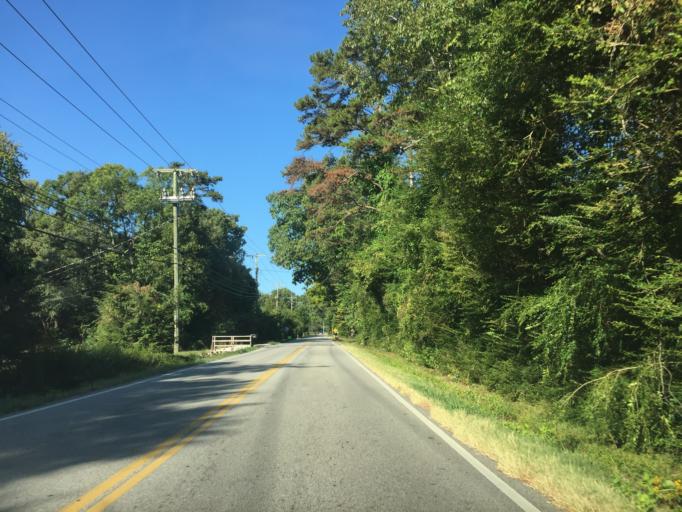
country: US
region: Tennessee
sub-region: Hamilton County
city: Harrison
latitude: 35.1216
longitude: -85.0952
